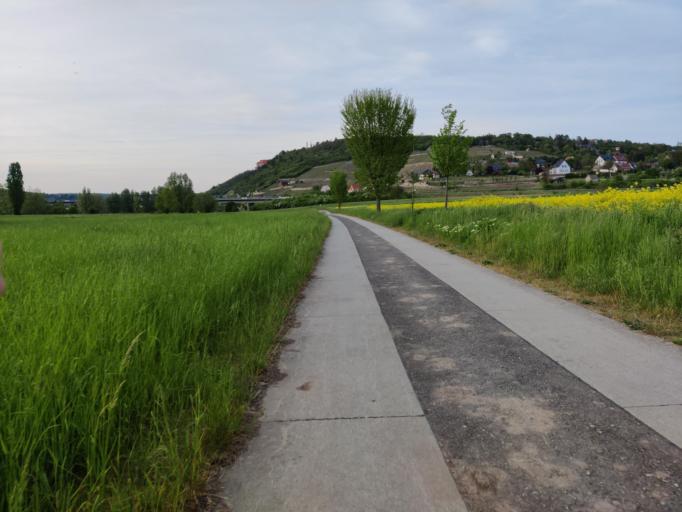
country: DE
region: Saxony-Anhalt
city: Freyburg
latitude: 51.1980
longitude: 11.7768
